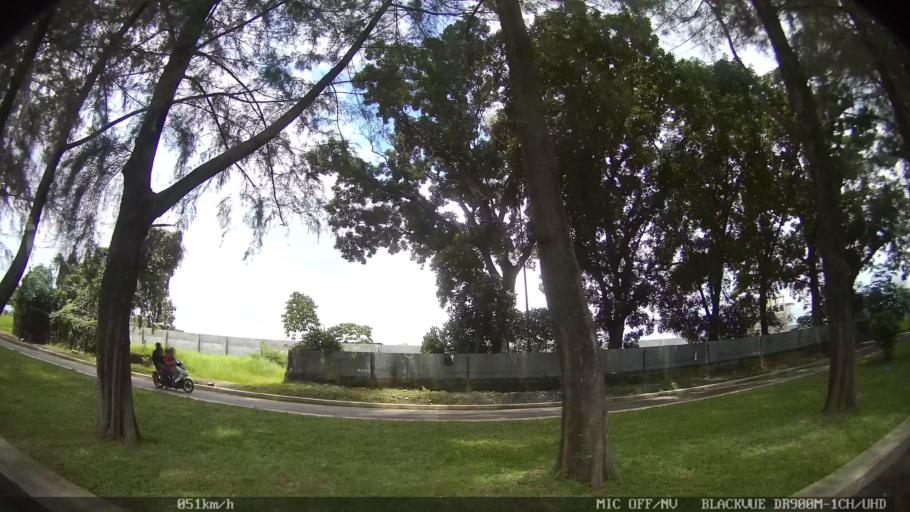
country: ID
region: North Sumatra
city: Medan
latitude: 3.6096
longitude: 98.7291
